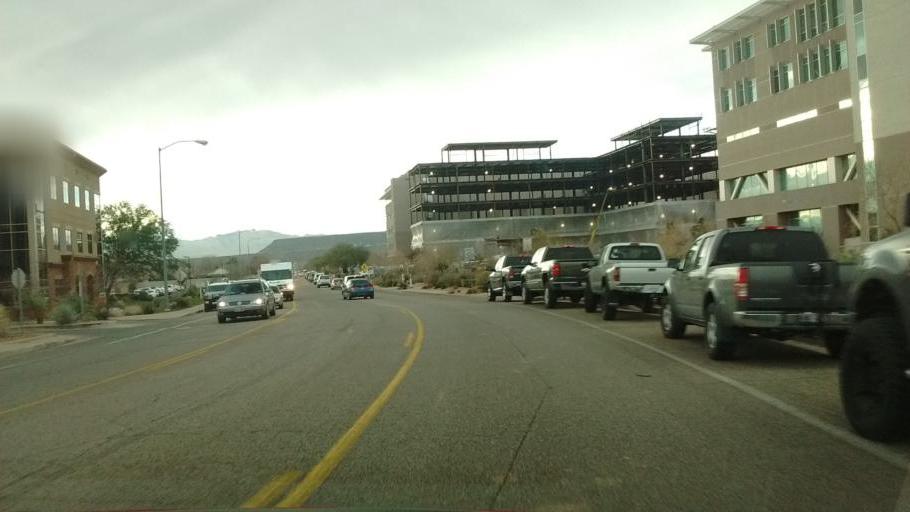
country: US
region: Utah
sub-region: Washington County
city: Saint George
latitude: 37.0963
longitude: -113.5512
